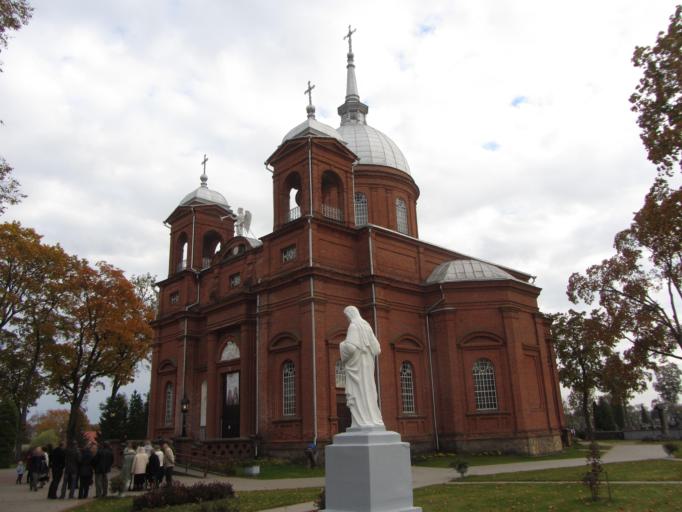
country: LT
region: Utenos apskritis
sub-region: Utena
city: Utena
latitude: 55.4943
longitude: 25.6049
